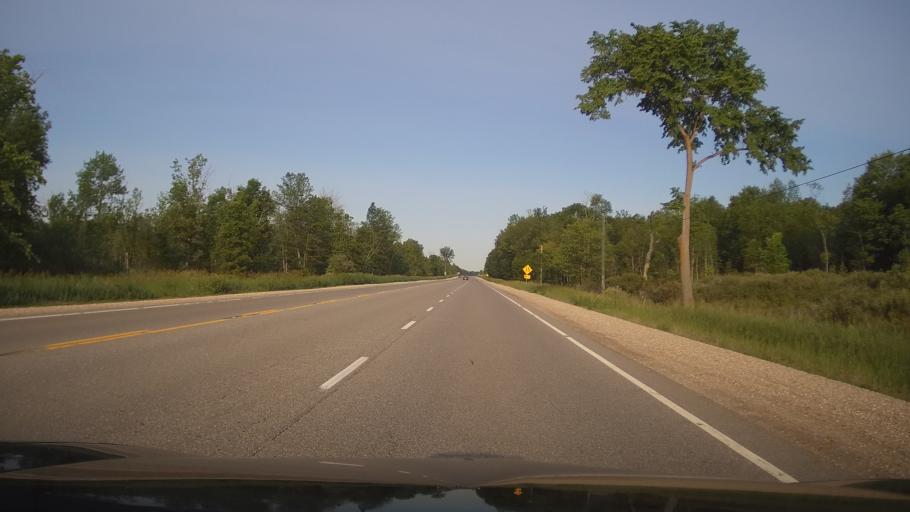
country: CA
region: Ontario
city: Perth
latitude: 44.8742
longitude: -76.3612
